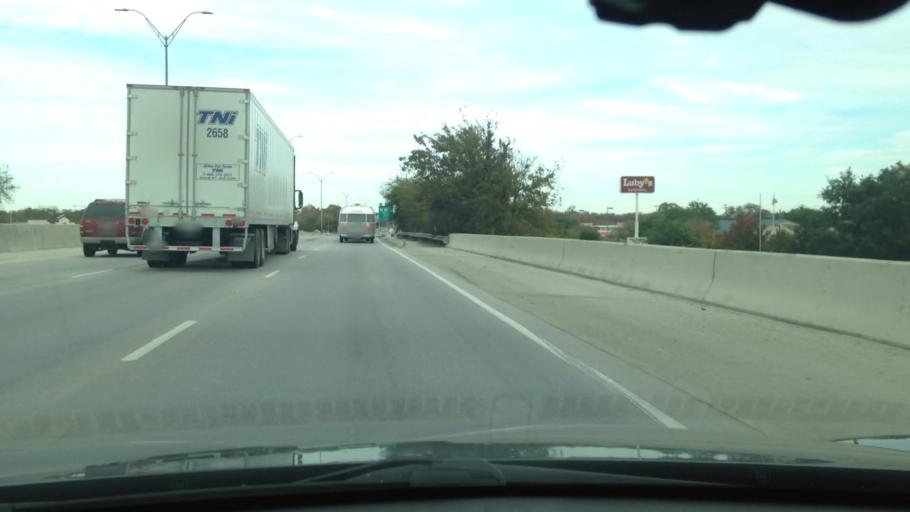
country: US
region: Texas
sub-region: Hays County
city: San Marcos
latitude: 29.8691
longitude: -97.9392
